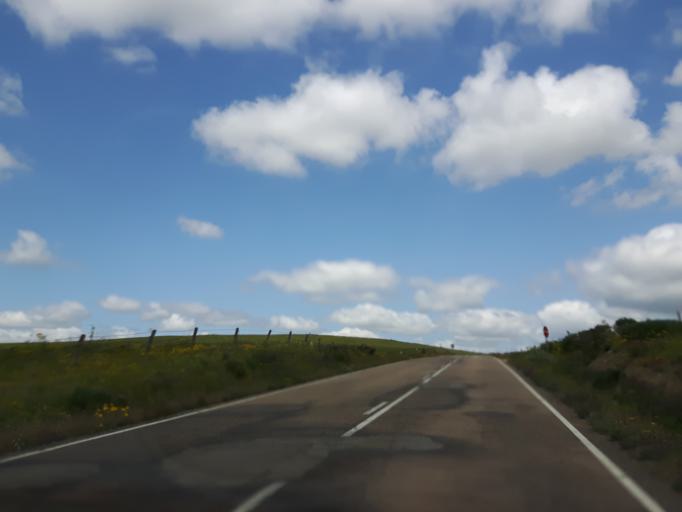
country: ES
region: Castille and Leon
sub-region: Provincia de Salamanca
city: Villar de la Yegua
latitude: 40.7173
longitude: -6.6947
